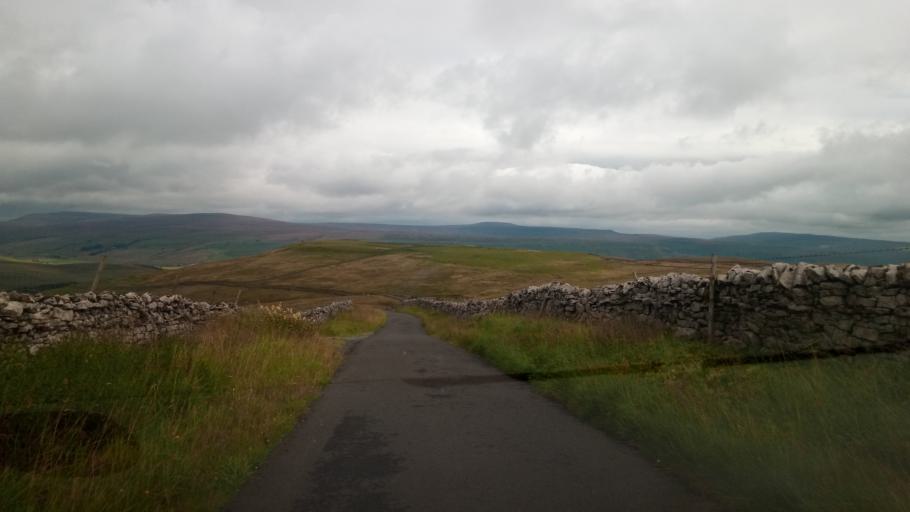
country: GB
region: England
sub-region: Cumbria
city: Kirkby Stephen
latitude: 54.3049
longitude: -2.3290
